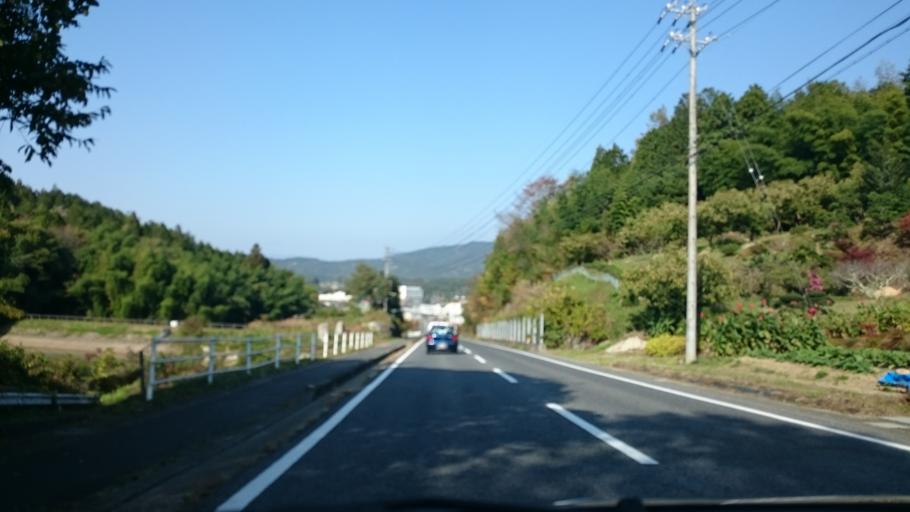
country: JP
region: Gifu
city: Nakatsugawa
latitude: 35.5154
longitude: 137.4764
